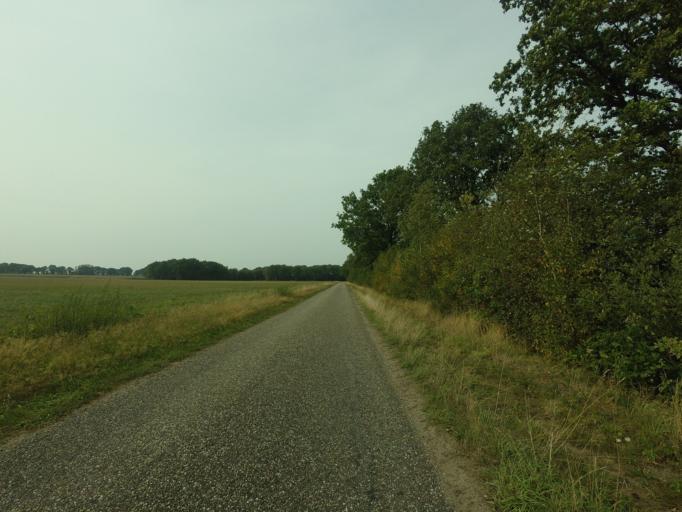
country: NL
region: Drenthe
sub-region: Gemeente Tynaarlo
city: Vries
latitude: 53.1088
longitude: 6.5450
